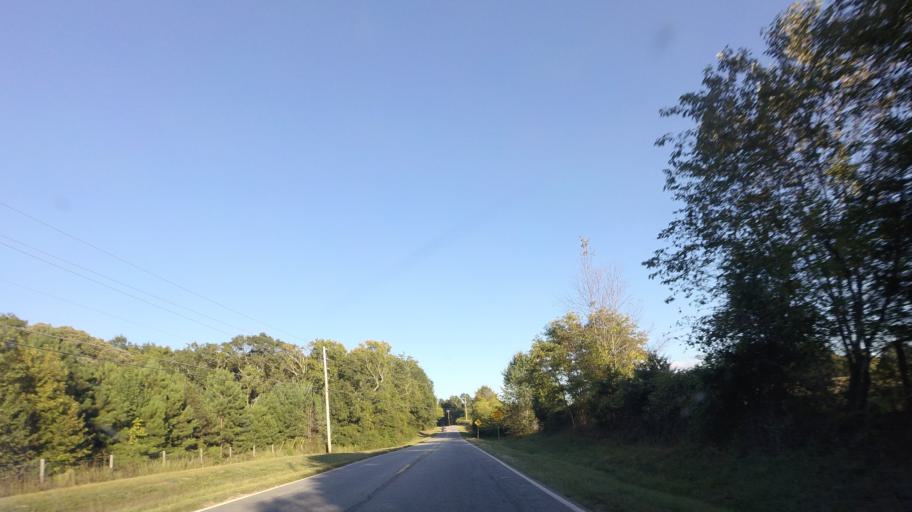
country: US
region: Georgia
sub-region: Spalding County
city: East Griffin
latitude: 33.2911
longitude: -84.1849
